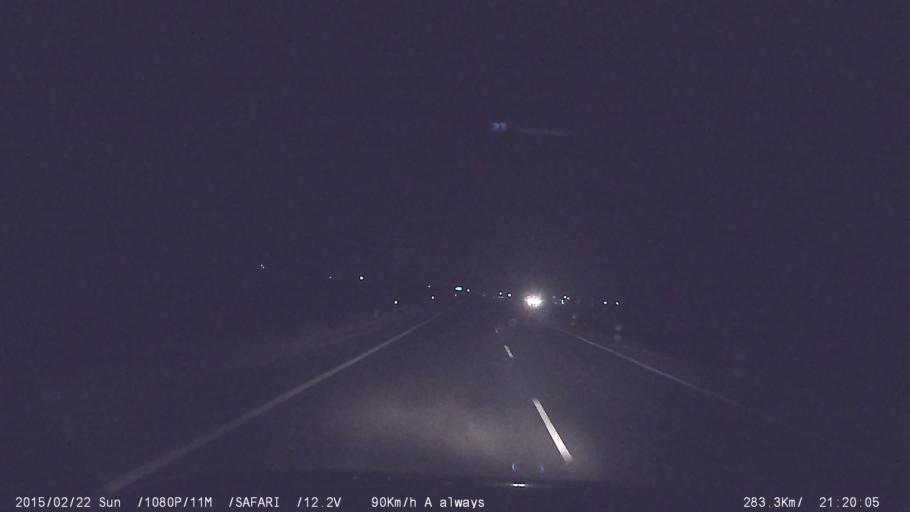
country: IN
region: Tamil Nadu
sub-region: Karur
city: Karur
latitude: 10.8517
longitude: 77.9794
